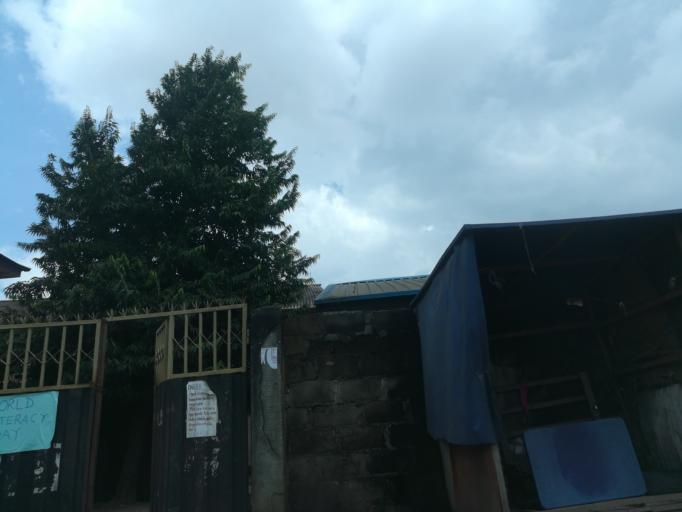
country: NG
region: Lagos
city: Mushin
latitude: 6.5272
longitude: 3.3566
